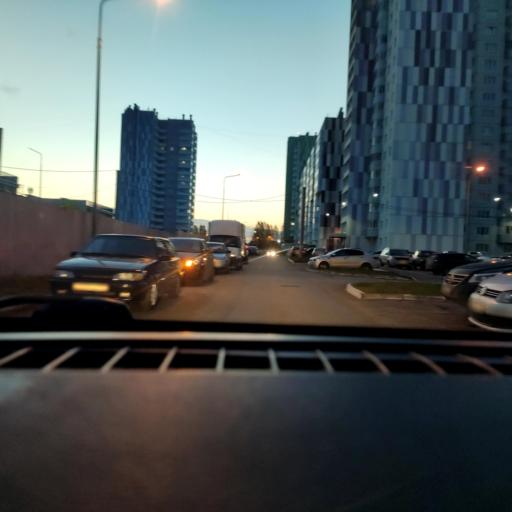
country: RU
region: Perm
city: Perm
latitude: 58.0534
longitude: 56.3482
